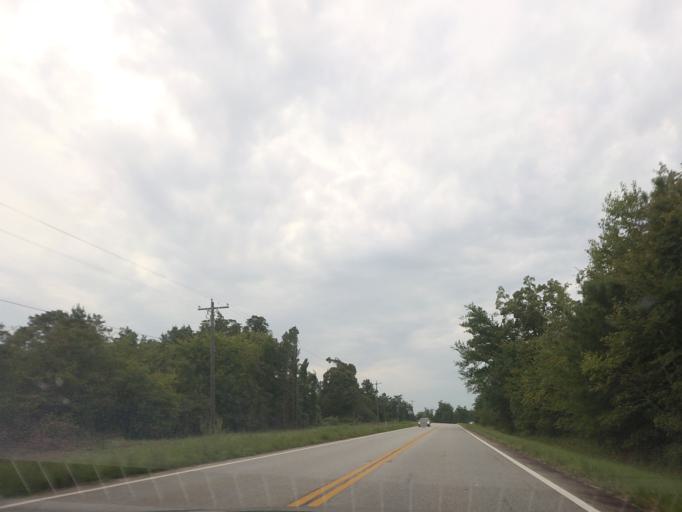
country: US
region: Georgia
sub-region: Twiggs County
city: Jeffersonville
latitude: 32.7512
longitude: -83.4419
